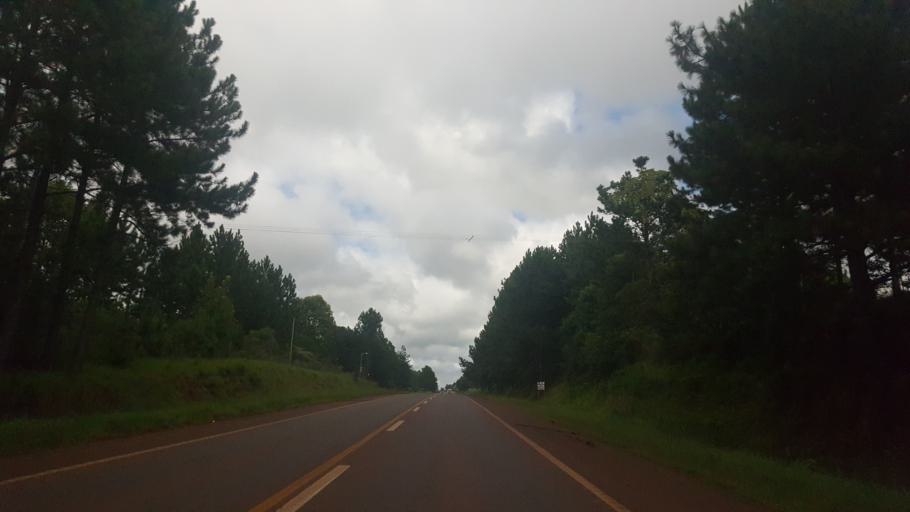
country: AR
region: Misiones
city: Aristobulo del Valle
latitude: -27.0854
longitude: -54.8012
